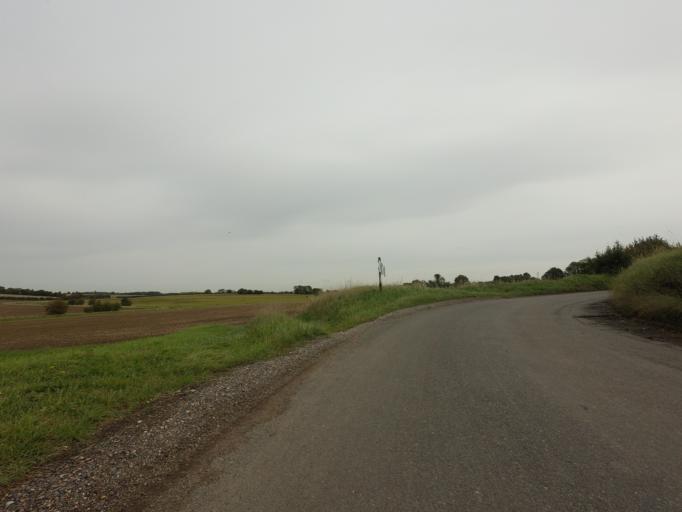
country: GB
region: England
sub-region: Hertfordshire
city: Reed
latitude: 51.9826
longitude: 0.0391
